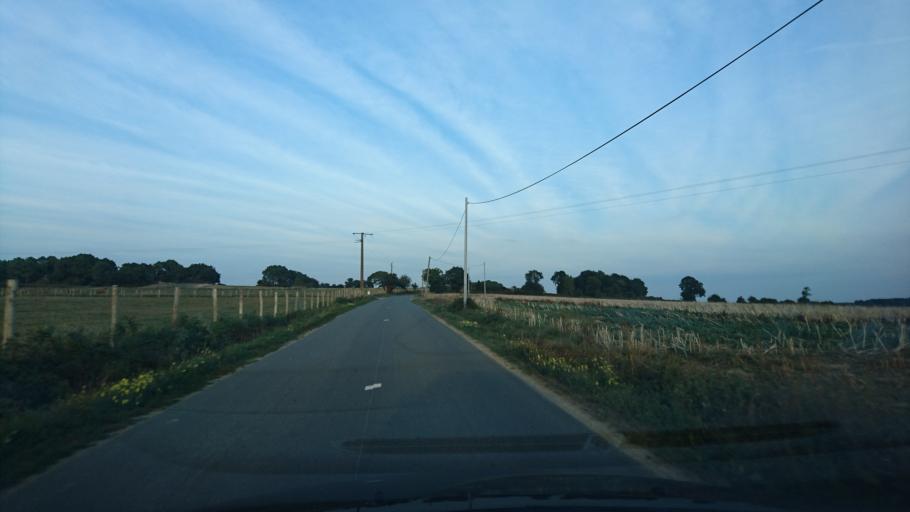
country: FR
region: Brittany
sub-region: Departement d'Ille-et-Vilaine
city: Sixt-sur-Aff
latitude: 47.8083
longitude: -2.0505
